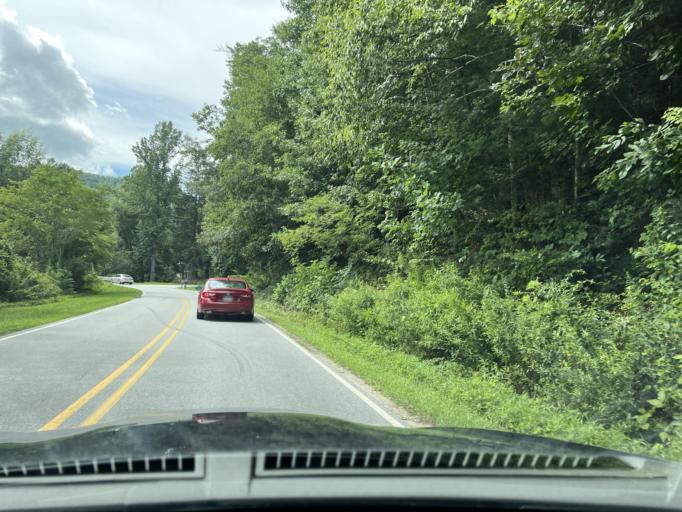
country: US
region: North Carolina
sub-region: Henderson County
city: Fruitland
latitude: 35.4055
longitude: -82.4068
